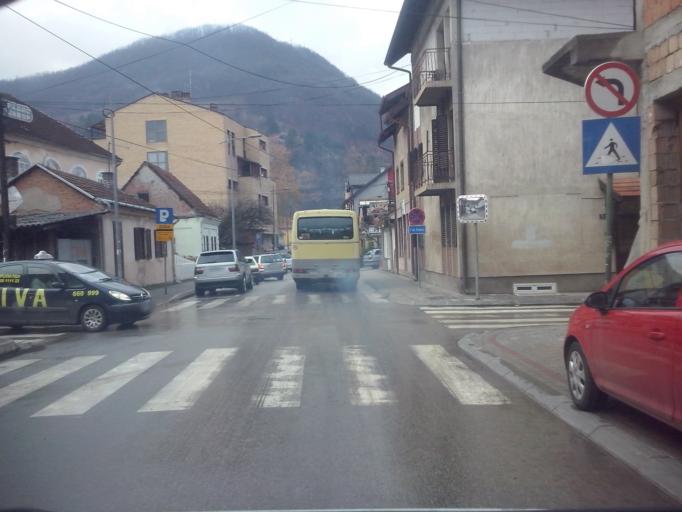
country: RS
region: Central Serbia
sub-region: Moravicki Okrug
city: Ivanjica
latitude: 43.5825
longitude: 20.2273
